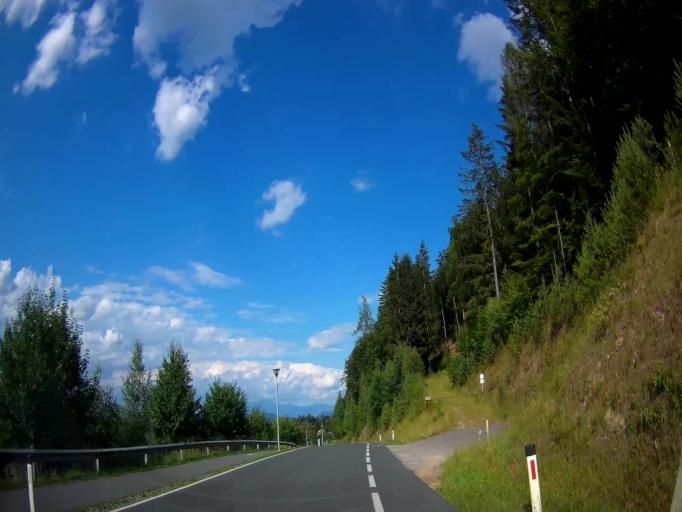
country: AT
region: Carinthia
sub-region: Politischer Bezirk Volkermarkt
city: Eberndorf
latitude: 46.6018
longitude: 14.5887
